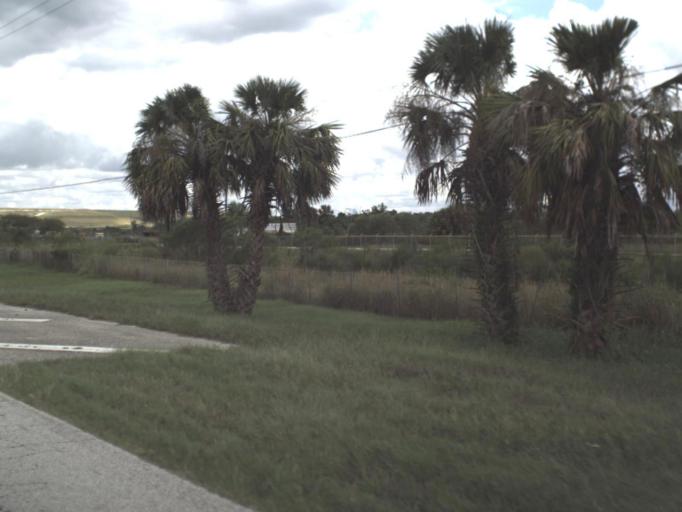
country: US
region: Florida
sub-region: Polk County
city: Bartow
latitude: 27.8982
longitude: -81.8854
